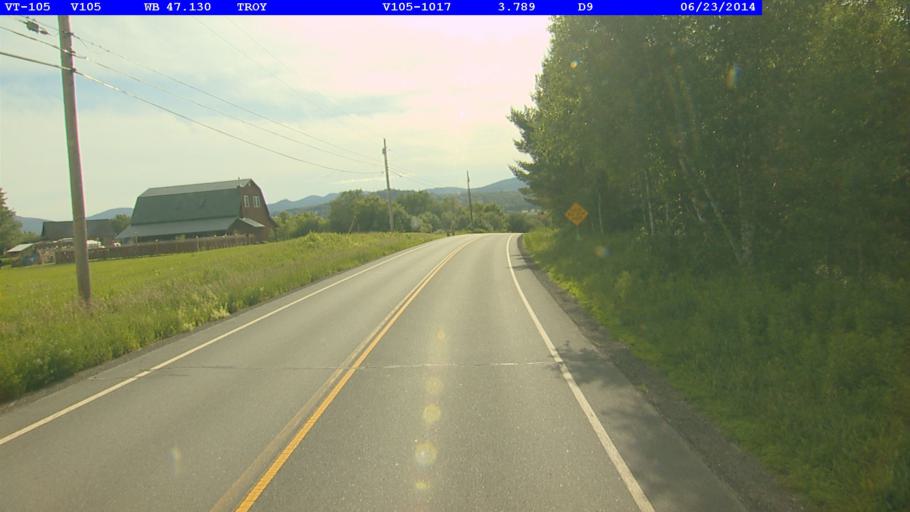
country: US
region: Vermont
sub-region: Orleans County
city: Newport
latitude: 44.9916
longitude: -72.3821
